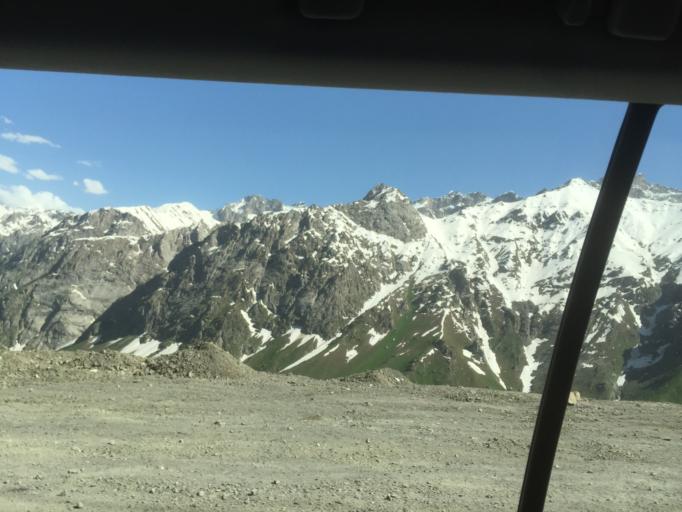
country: TJ
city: Tagob
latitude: 39.0592
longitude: 68.7034
